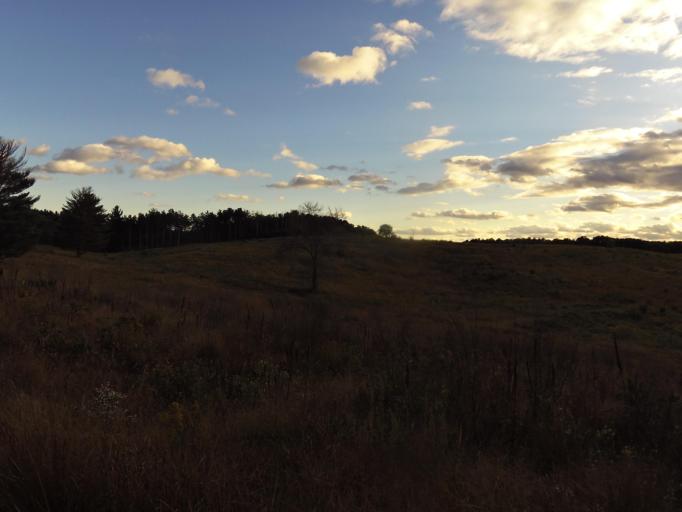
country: US
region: Minnesota
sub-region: Washington County
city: Lake Saint Croix Beach
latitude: 44.9382
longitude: -92.7859
